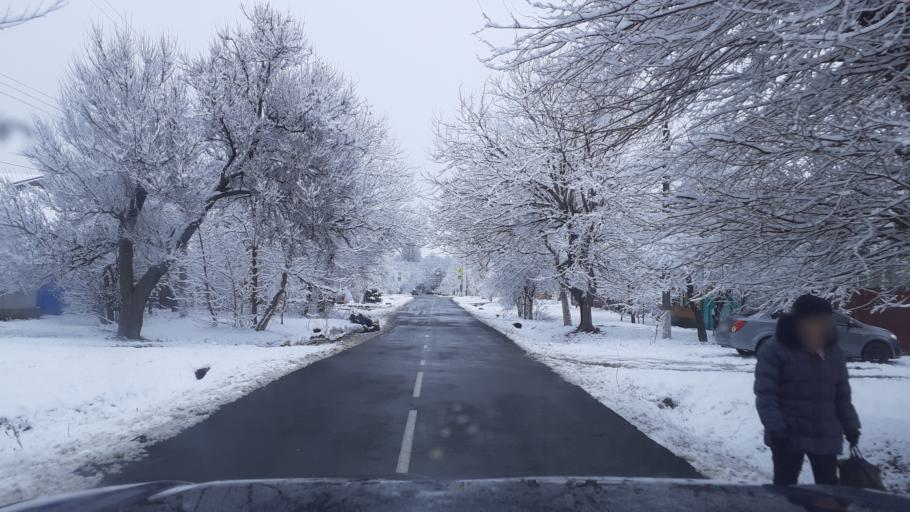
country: RU
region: Adygeya
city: Maykop
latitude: 44.6136
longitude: 40.1179
